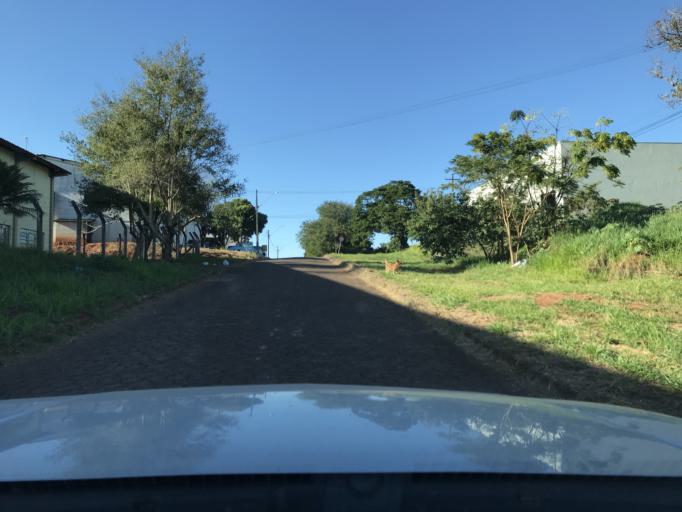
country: BR
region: Parana
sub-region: Ipora
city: Ipora
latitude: -23.9967
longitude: -53.7057
